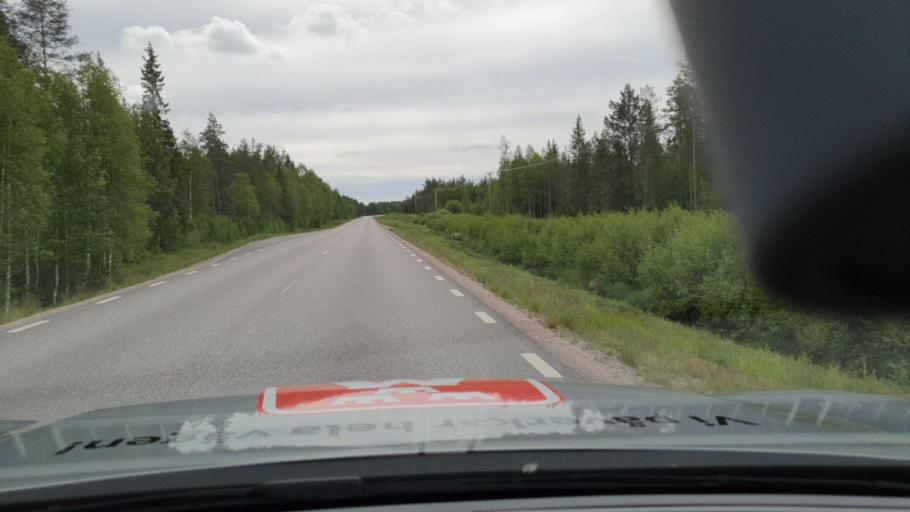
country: SE
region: Norrbotten
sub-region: Kalix Kommun
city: Kalix
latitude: 65.8811
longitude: 23.4799
